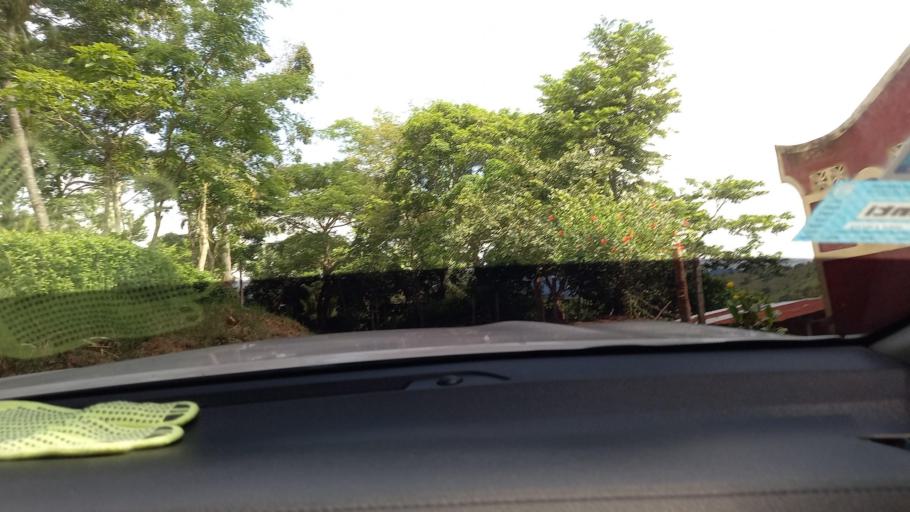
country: NI
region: Jinotega
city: San Jose de Bocay
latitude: 13.4060
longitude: -85.7015
